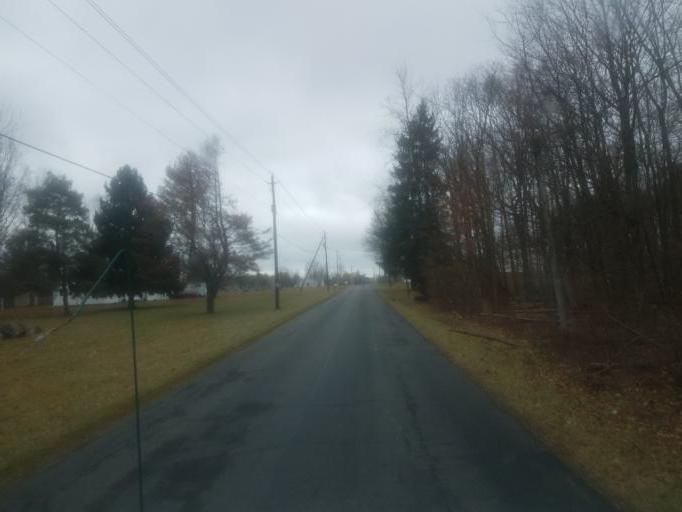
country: US
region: Ohio
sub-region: Crawford County
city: Galion
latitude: 40.7688
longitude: -82.8201
